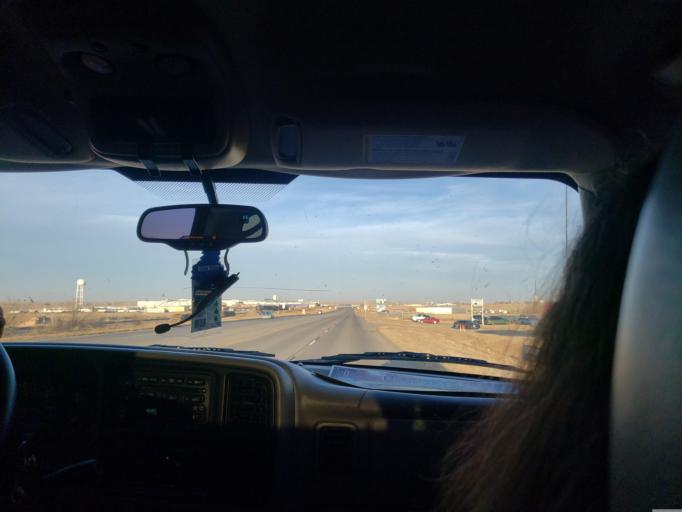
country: US
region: Oklahoma
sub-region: Texas County
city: Guymon
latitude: 36.7011
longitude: -101.4516
